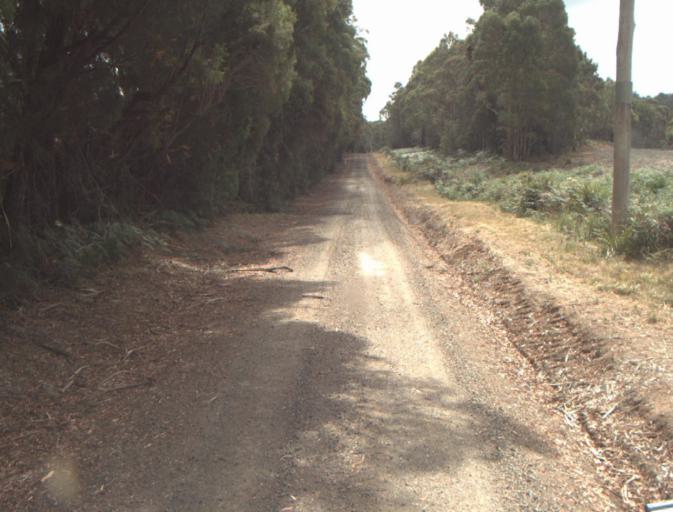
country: AU
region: Tasmania
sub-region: Launceston
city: Mayfield
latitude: -41.2783
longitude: 147.0522
